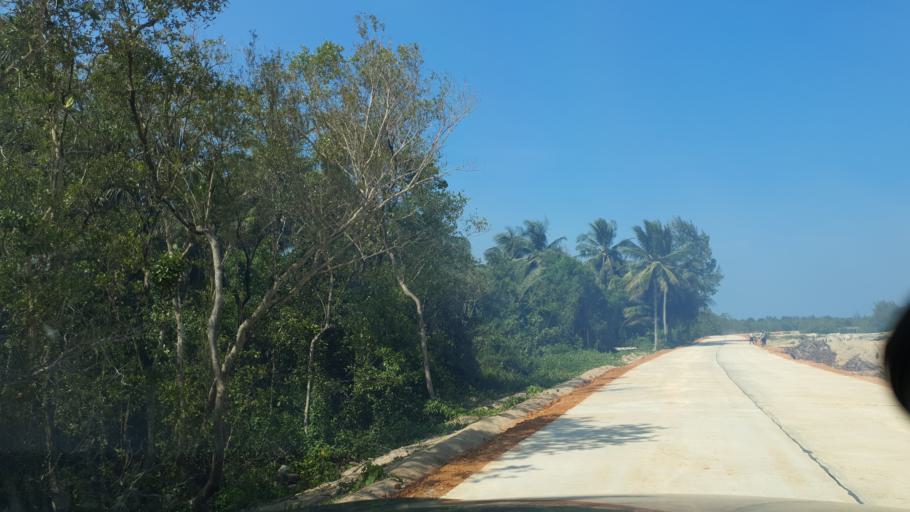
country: TH
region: Surat Thani
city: Tha Chana
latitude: 9.5895
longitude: 99.2077
